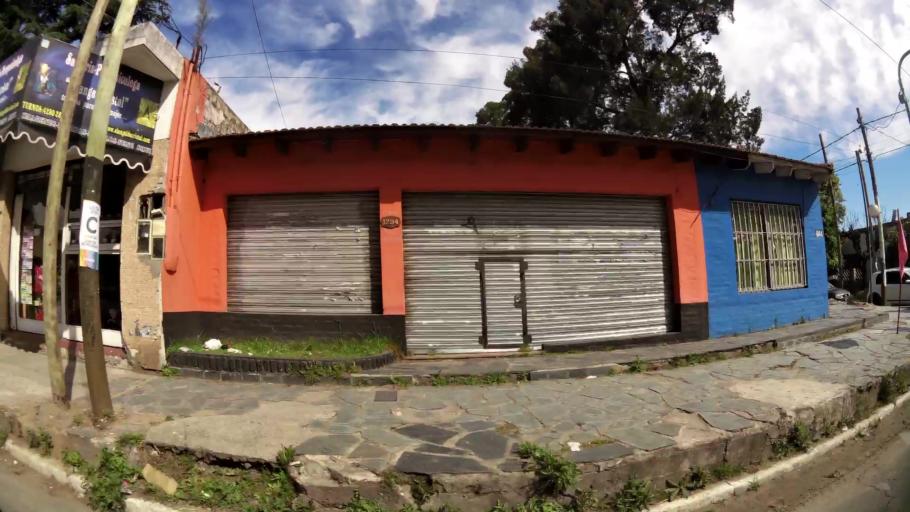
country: AR
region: Buenos Aires
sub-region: Partido de Quilmes
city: Quilmes
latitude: -34.7716
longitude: -58.2975
